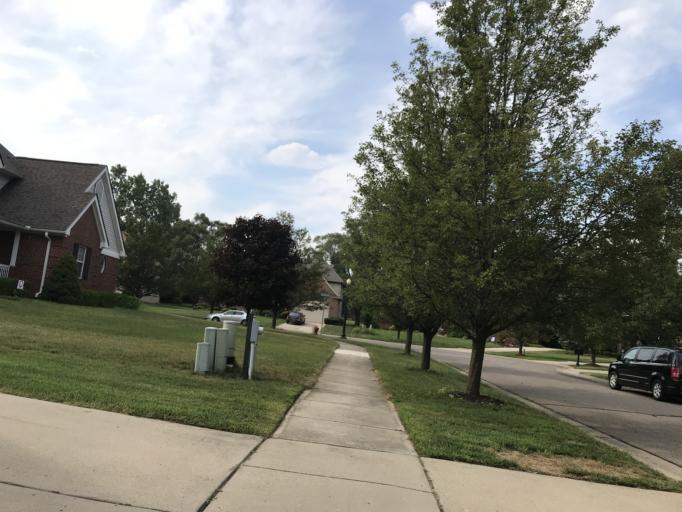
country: US
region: Michigan
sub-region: Oakland County
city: Franklin
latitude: 42.4971
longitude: -83.3329
